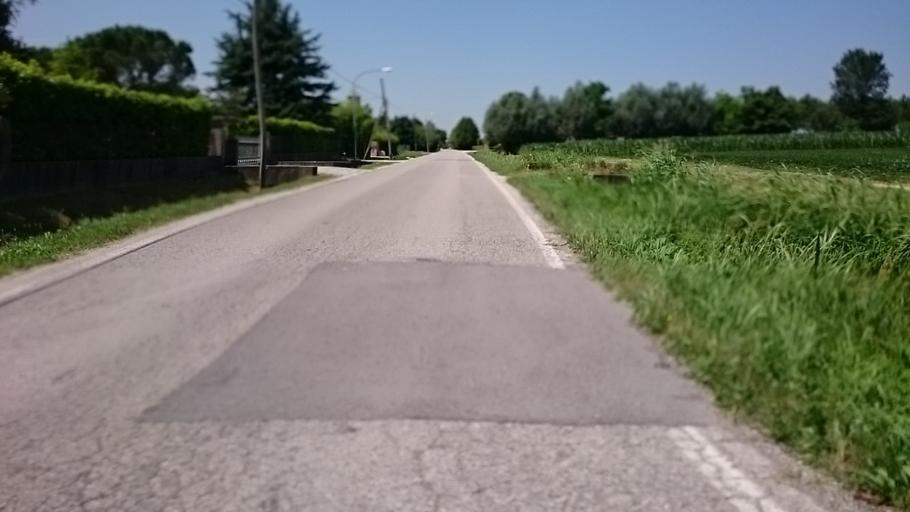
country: IT
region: Veneto
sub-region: Provincia di Venezia
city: Sant'Angelo
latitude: 45.5169
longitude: 12.0040
